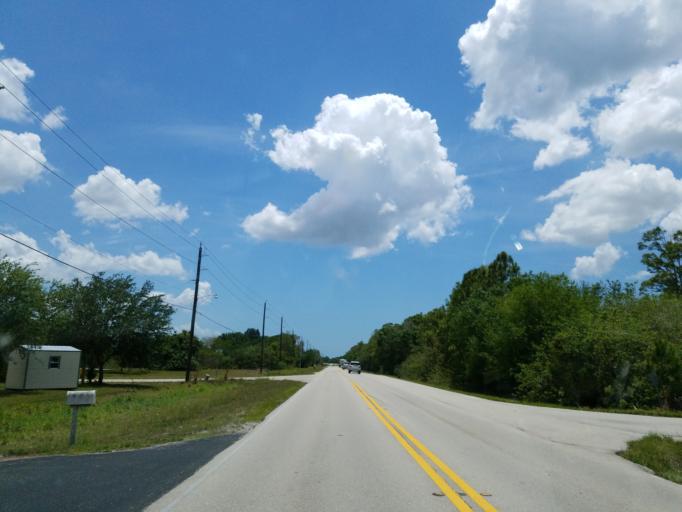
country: US
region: Florida
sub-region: Charlotte County
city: Harbour Heights
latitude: 27.0526
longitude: -82.0304
